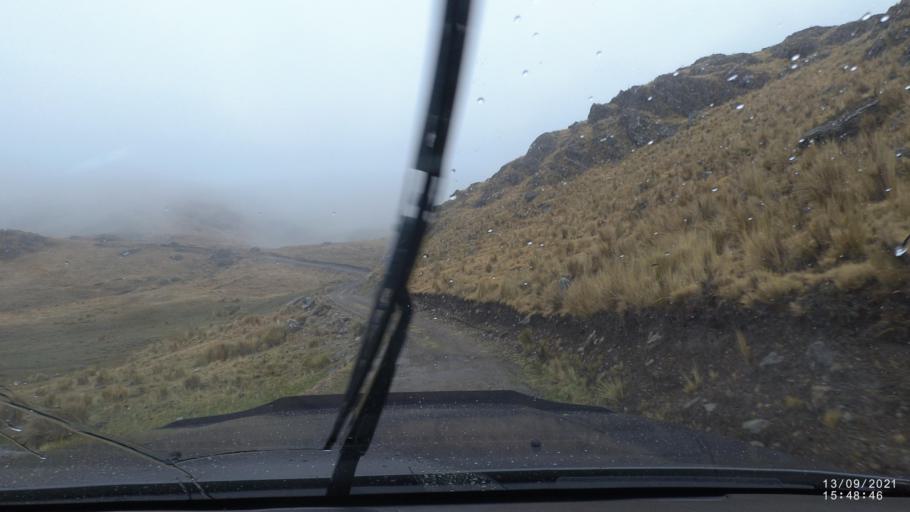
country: BO
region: Cochabamba
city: Colomi
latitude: -17.3100
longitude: -65.7150
